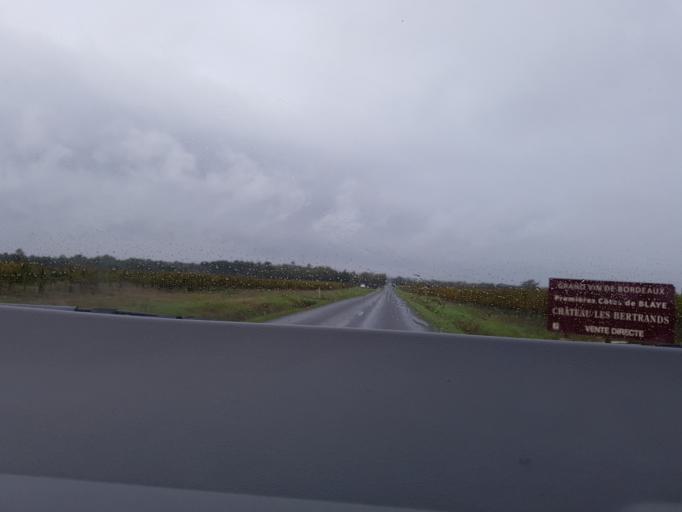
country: FR
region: Aquitaine
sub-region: Departement de la Gironde
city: Reignac
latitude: 45.2377
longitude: -0.5213
